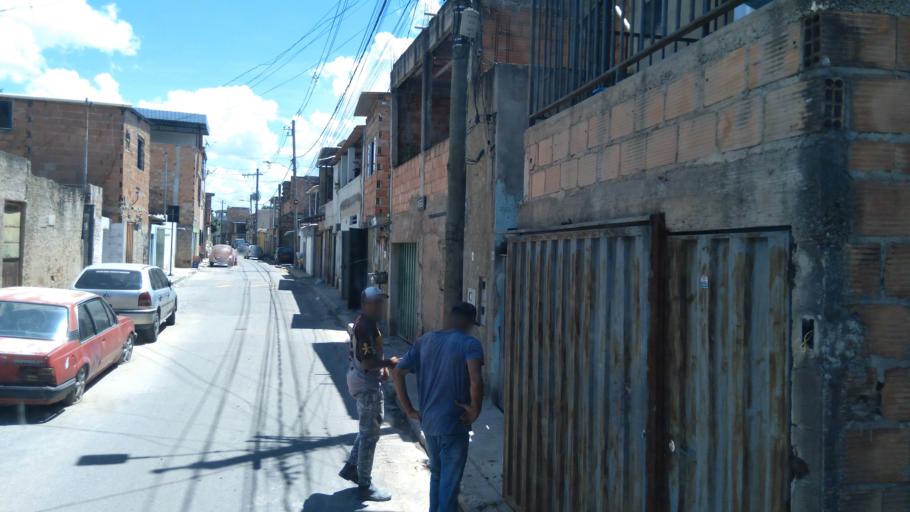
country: BR
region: Minas Gerais
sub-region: Santa Luzia
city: Santa Luzia
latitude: -19.8356
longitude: -43.8950
